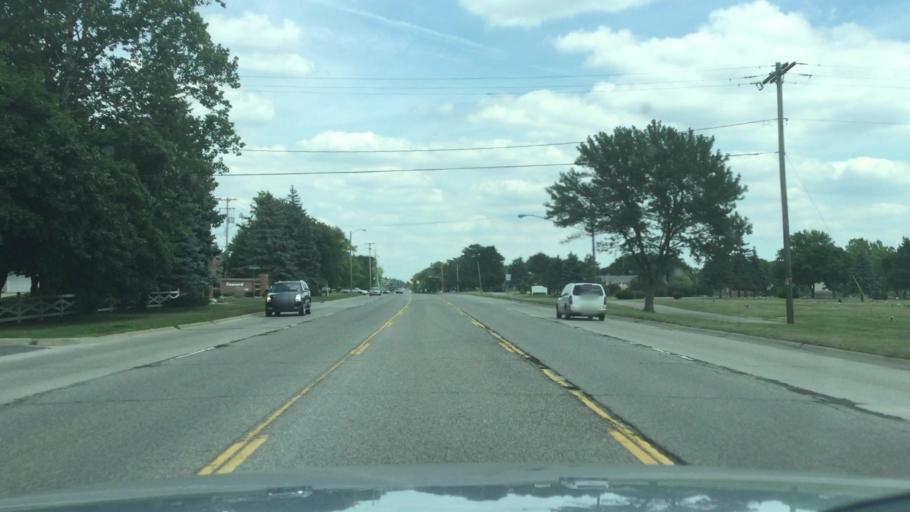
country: US
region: Michigan
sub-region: Genesee County
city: Grand Blanc
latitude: 42.9440
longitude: -83.6741
